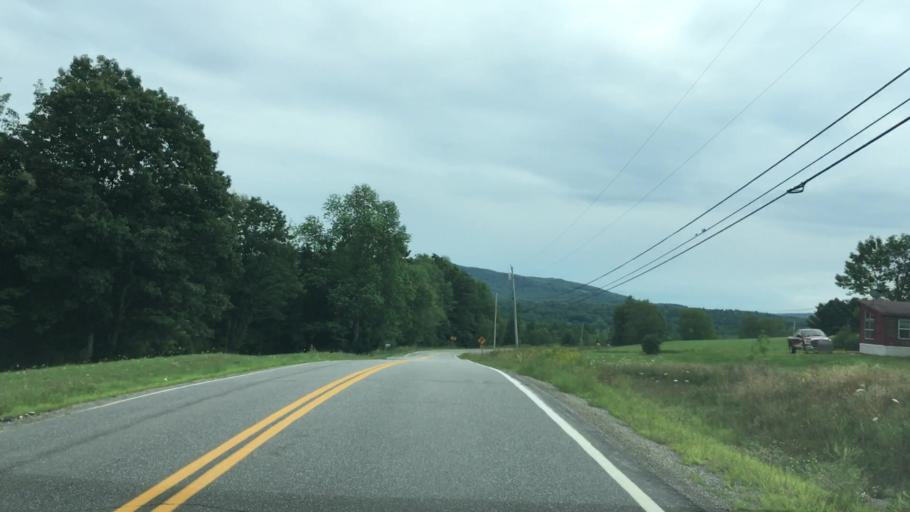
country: US
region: Maine
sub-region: Waldo County
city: Lincolnville
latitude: 44.3100
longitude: -69.0874
